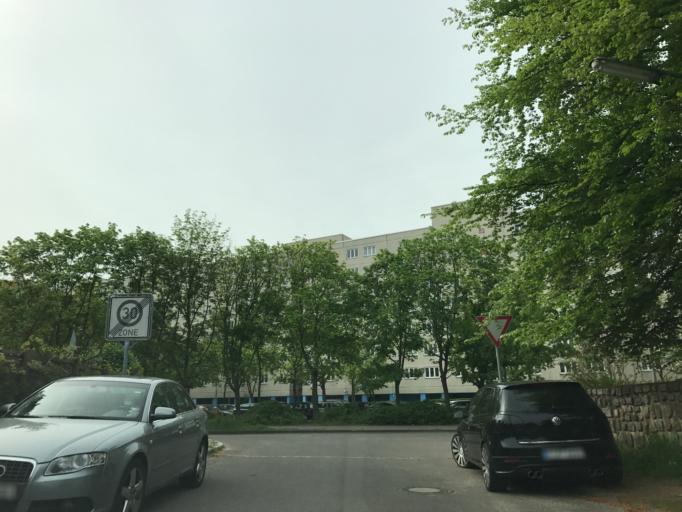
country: DE
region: Berlin
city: Wilhelmstadt
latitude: 52.5241
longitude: 13.1649
